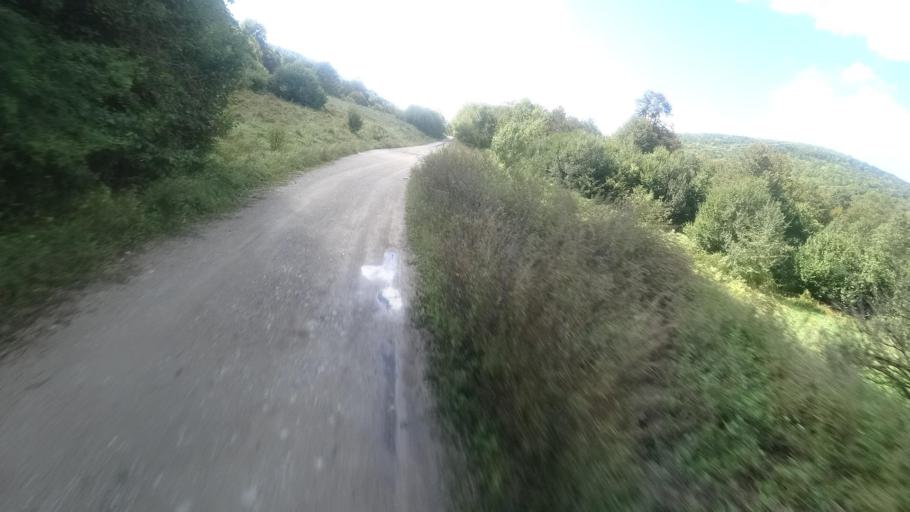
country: BA
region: Federation of Bosnia and Herzegovina
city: Ostrozac
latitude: 44.8371
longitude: 16.0071
